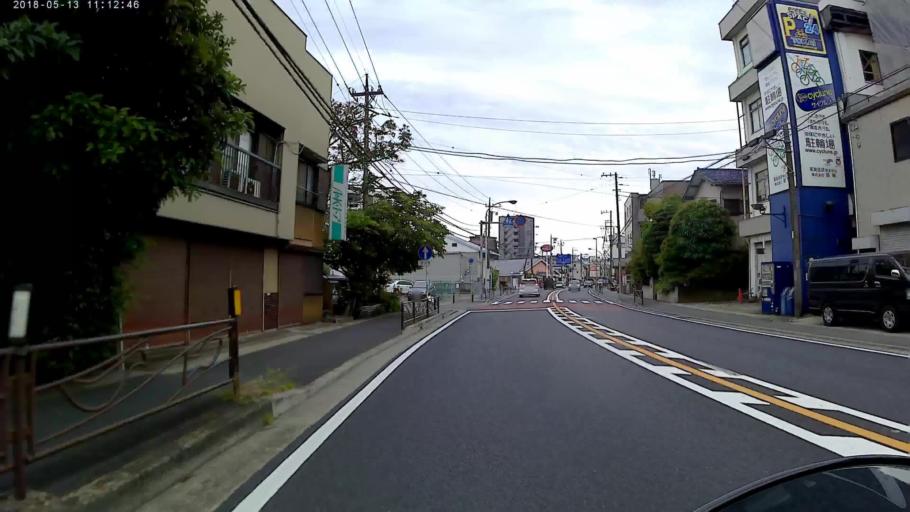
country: JP
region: Kanagawa
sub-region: Kawasaki-shi
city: Kawasaki
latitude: 35.5776
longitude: 139.6262
